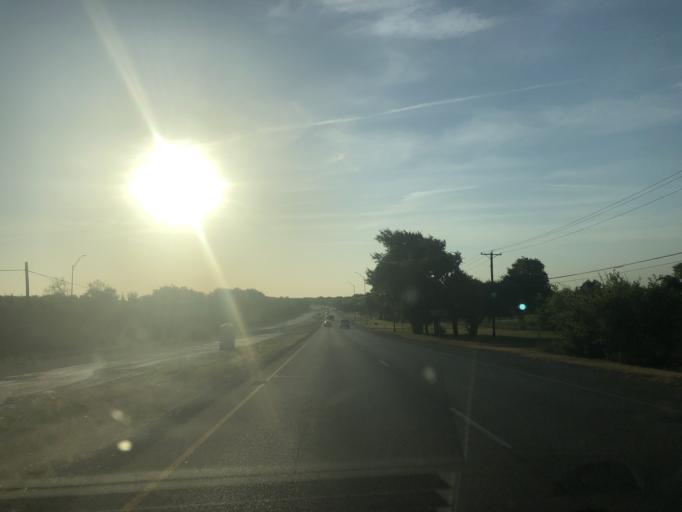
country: US
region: Texas
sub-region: Tarrant County
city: White Settlement
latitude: 32.7206
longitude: -97.5178
